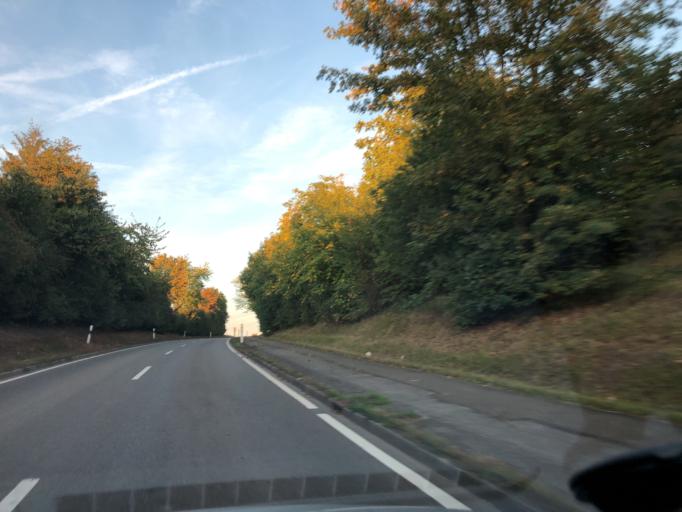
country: DE
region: Baden-Wuerttemberg
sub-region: Regierungsbezirk Stuttgart
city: Freiberg am Neckar
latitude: 48.9136
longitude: 9.2316
